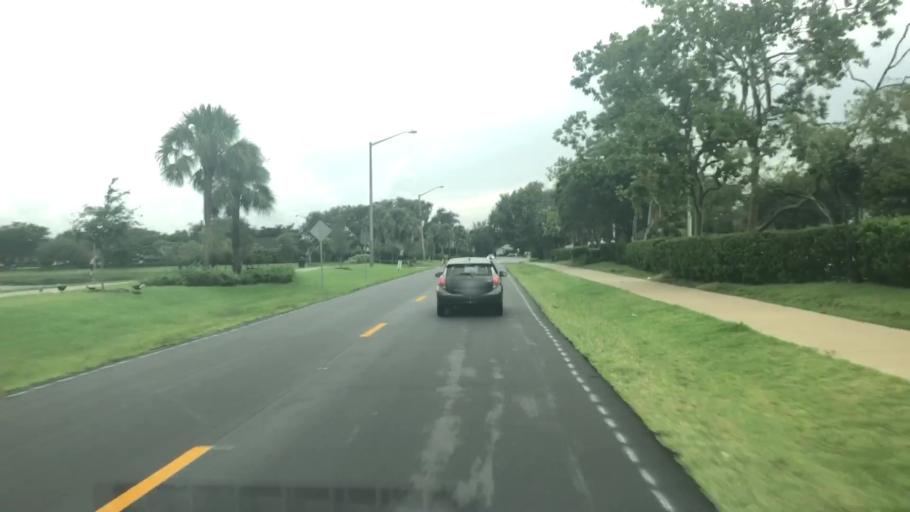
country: US
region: Florida
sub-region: Palm Beach County
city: Boca Pointe
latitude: 26.2978
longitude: -80.1847
